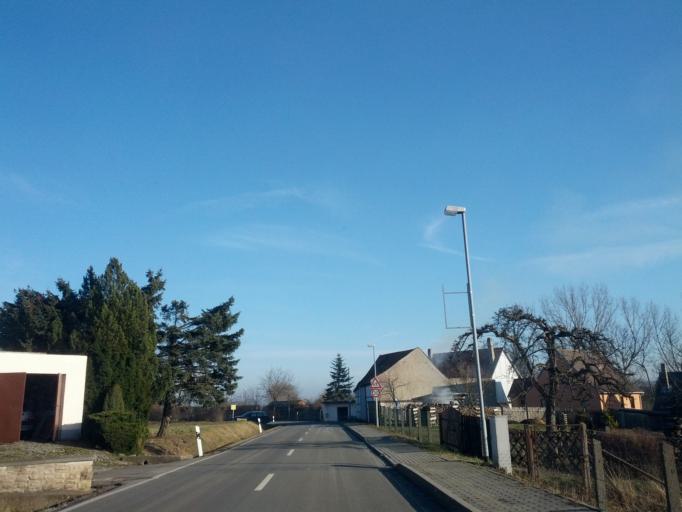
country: DE
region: Thuringia
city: Schonstedt
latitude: 51.0884
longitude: 10.5752
